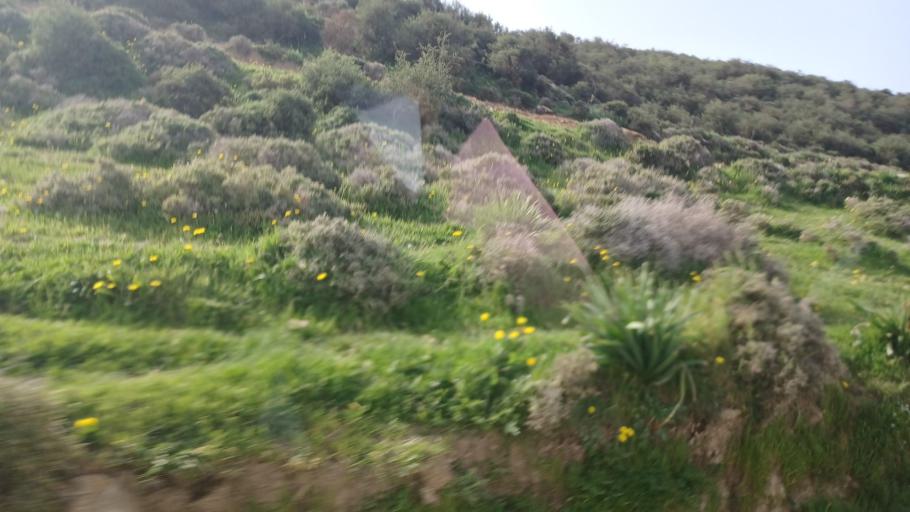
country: CY
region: Pafos
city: Polis
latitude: 34.9936
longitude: 32.3485
